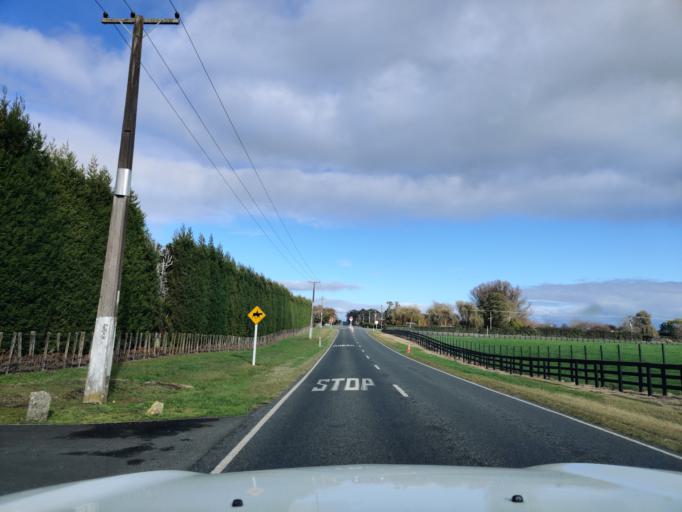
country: NZ
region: Waikato
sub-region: Waipa District
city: Cambridge
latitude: -37.8587
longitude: 175.4391
